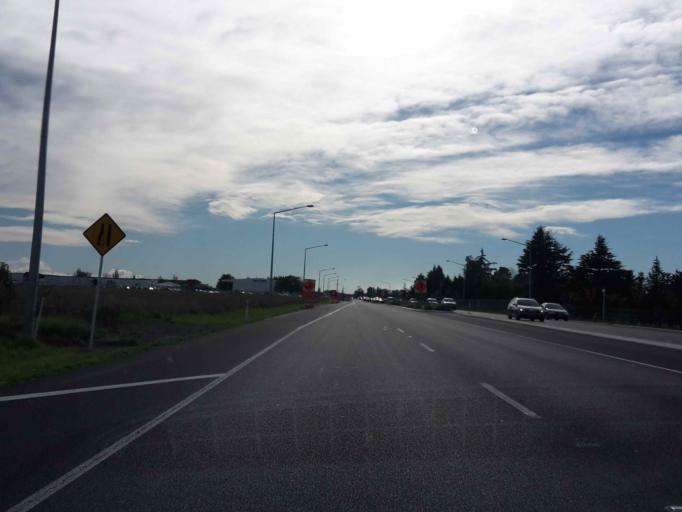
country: NZ
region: Canterbury
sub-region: Selwyn District
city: Prebbleton
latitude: -43.5004
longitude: 172.5455
